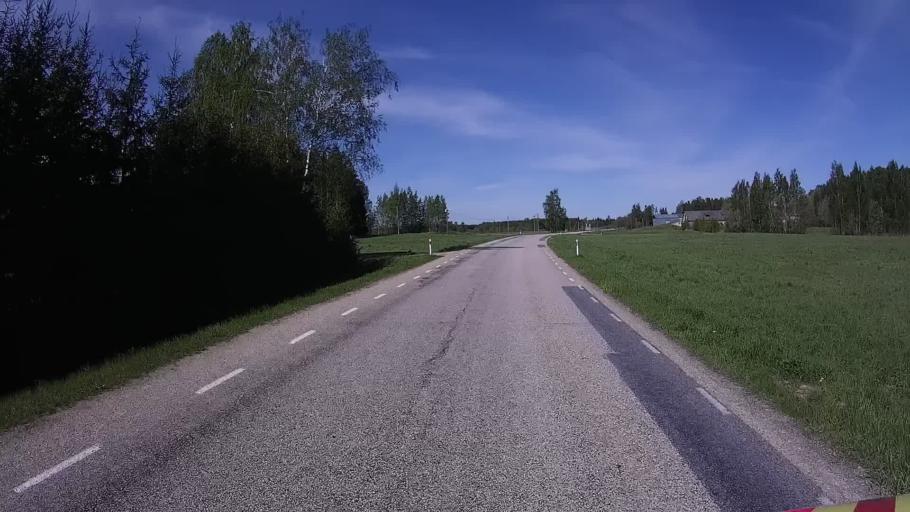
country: EE
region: Polvamaa
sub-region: Raepina vald
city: Rapina
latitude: 57.9666
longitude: 27.5373
